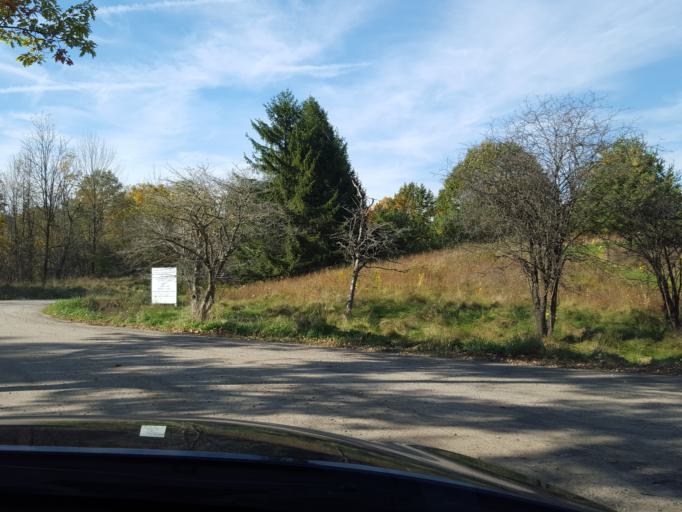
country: CA
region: Ontario
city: Ancaster
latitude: 43.2490
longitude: -79.9937
